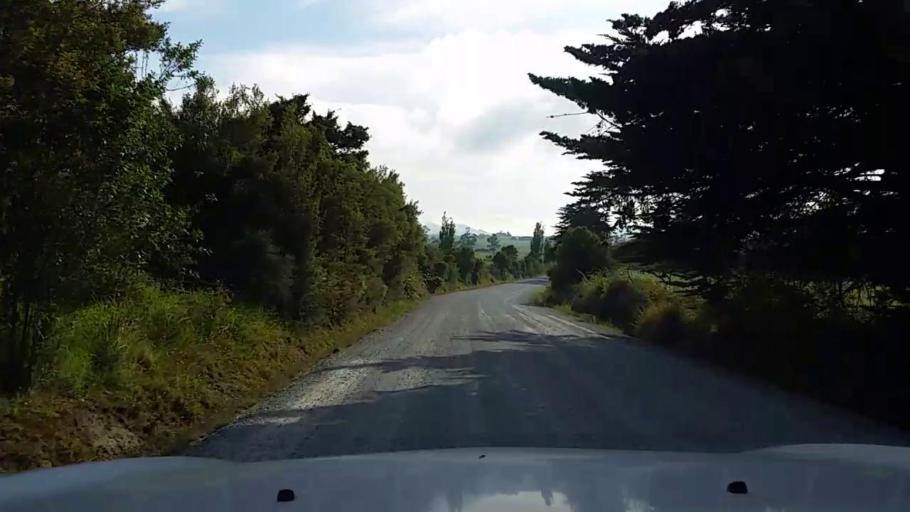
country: NZ
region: Northland
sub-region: Whangarei
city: Maungatapere
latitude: -35.6843
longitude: 174.1866
